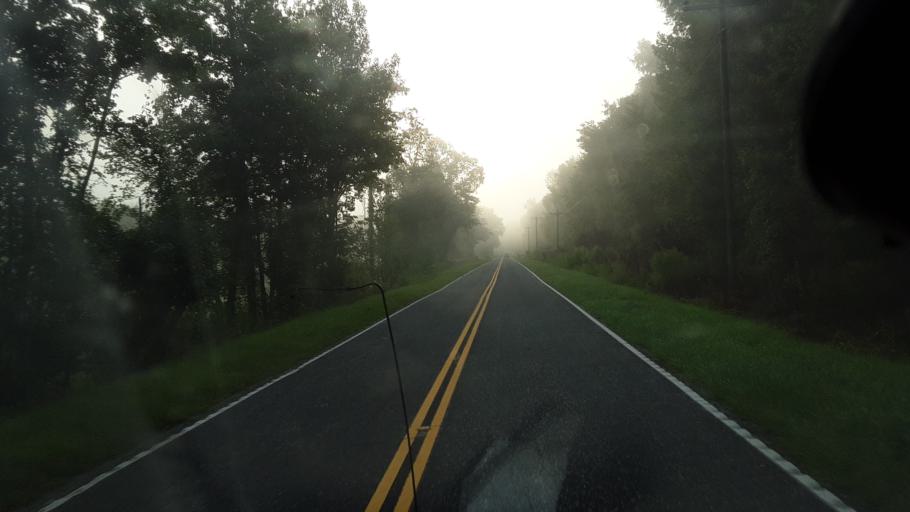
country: US
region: South Carolina
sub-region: Williamsburg County
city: Kingstree
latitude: 33.8236
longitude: -79.9601
